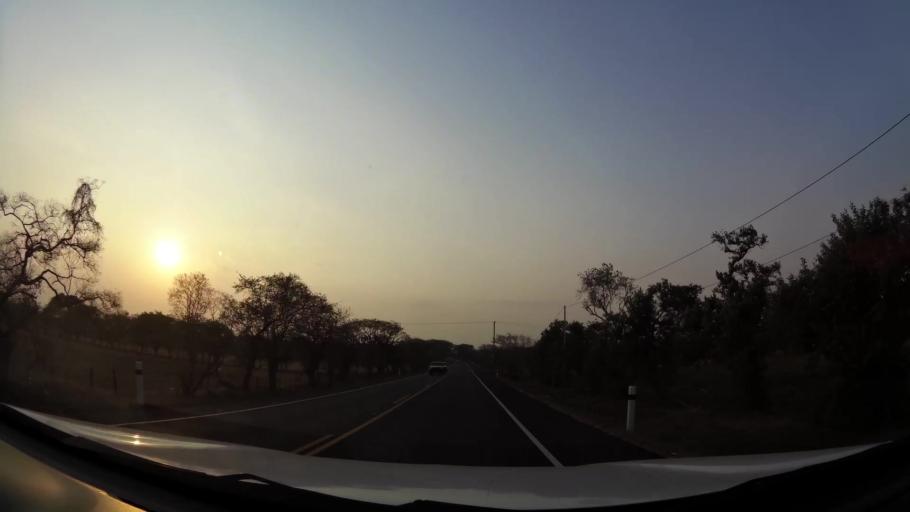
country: NI
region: Leon
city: Nagarote
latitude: 12.3127
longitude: -86.6062
